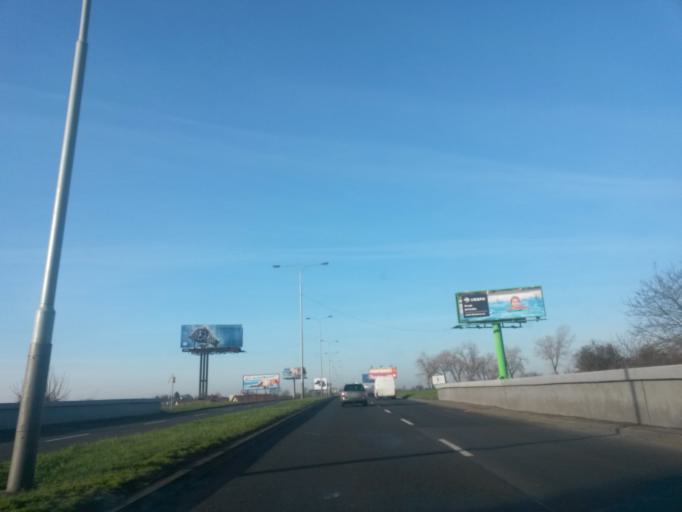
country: CZ
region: Praha
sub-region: Praha 12
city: Modrany
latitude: 50.0232
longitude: 14.3532
